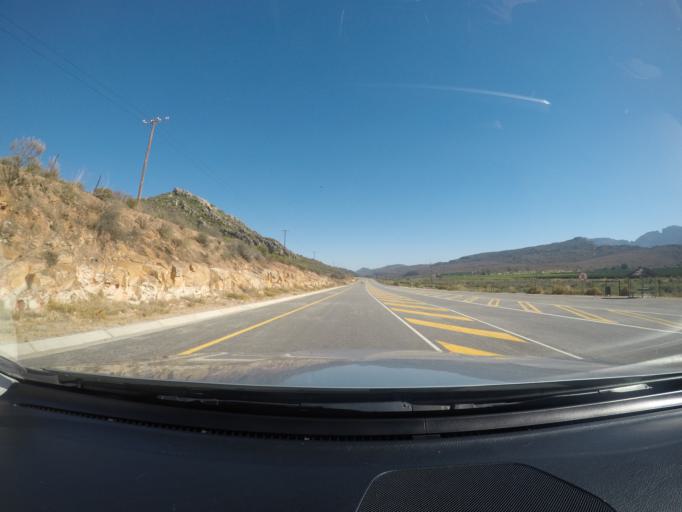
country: ZA
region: Western Cape
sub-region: West Coast District Municipality
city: Clanwilliam
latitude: -32.4467
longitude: 18.9583
